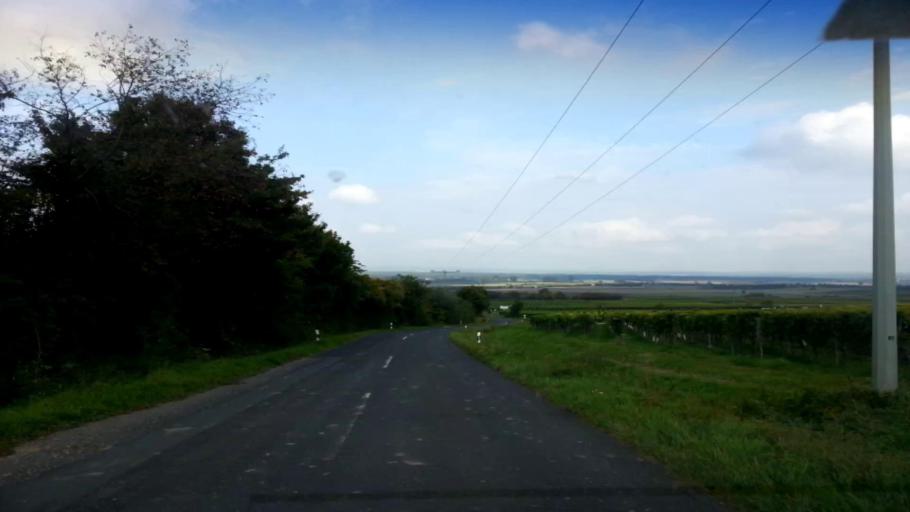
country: DE
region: Bavaria
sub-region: Regierungsbezirk Unterfranken
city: Rodelsee
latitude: 49.7308
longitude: 10.2722
